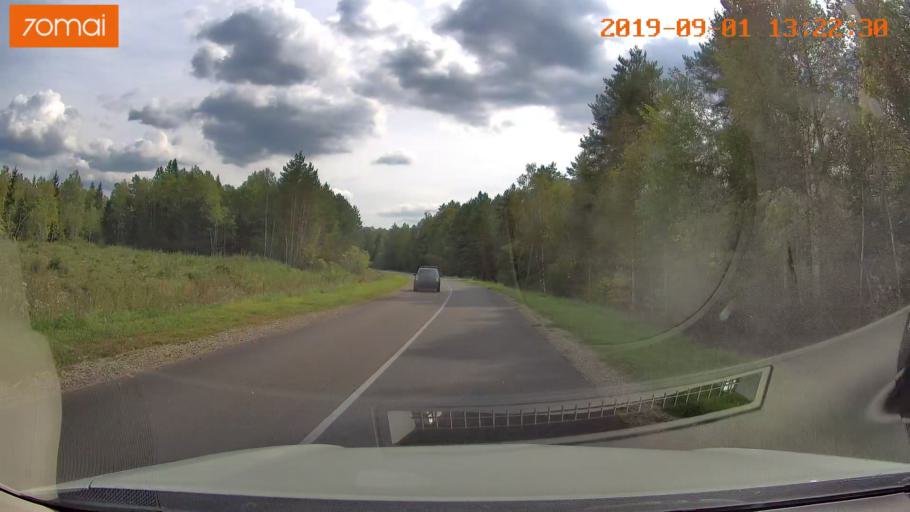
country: RU
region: Kaluga
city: Maloyaroslavets
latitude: 54.8893
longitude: 36.5231
